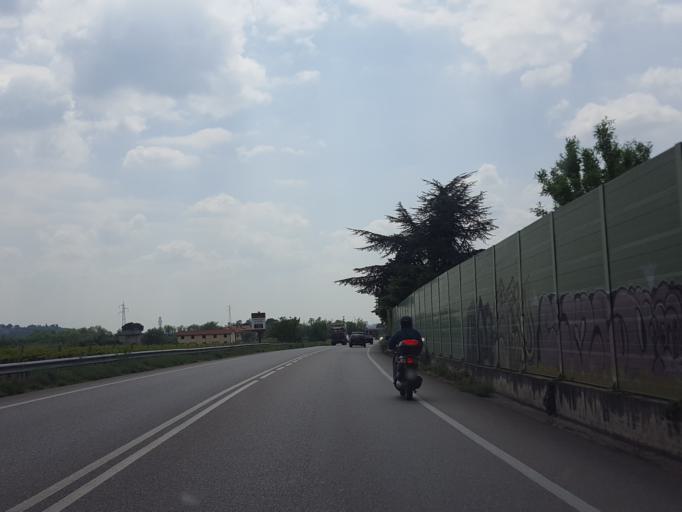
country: IT
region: Veneto
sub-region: Provincia di Verona
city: Poiano
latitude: 45.4965
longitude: 11.0208
